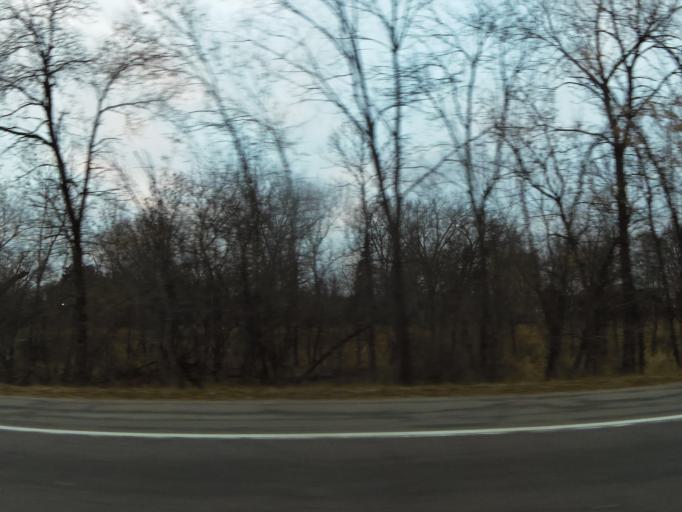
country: US
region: Minnesota
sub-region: Washington County
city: Birchwood
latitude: 45.0539
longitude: -92.9650
